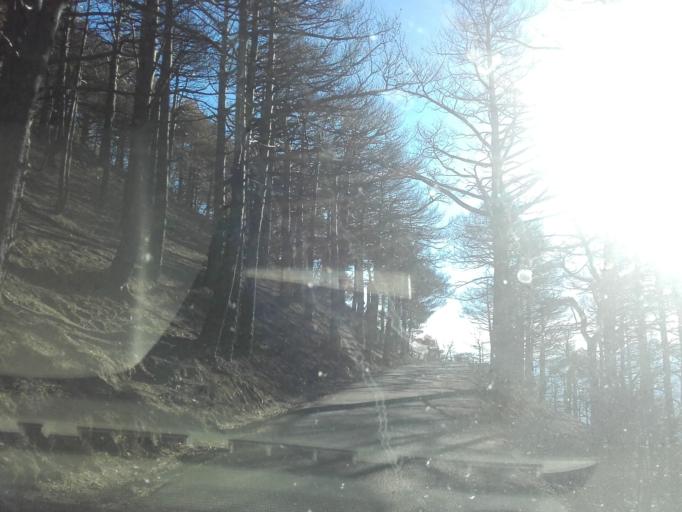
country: IT
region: Piedmont
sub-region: Provincia di Torino
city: Mompantero
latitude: 45.1620
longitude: 7.0432
